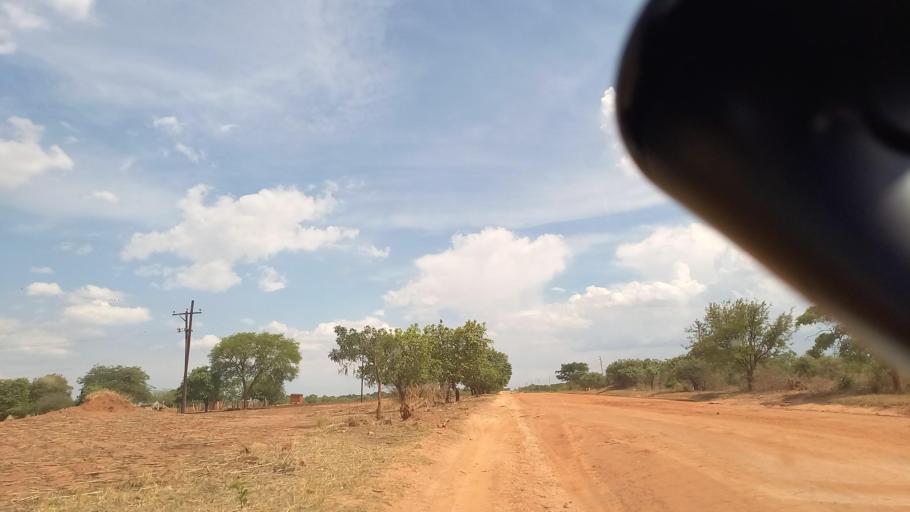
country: ZM
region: Lusaka
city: Kafue
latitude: -16.1369
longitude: 28.0511
